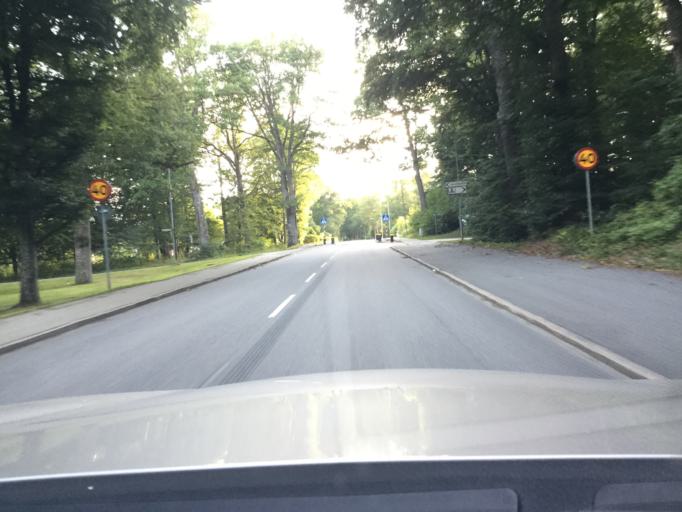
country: SE
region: Kronoberg
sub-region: Almhults Kommun
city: AElmhult
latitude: 56.6452
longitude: 14.2265
